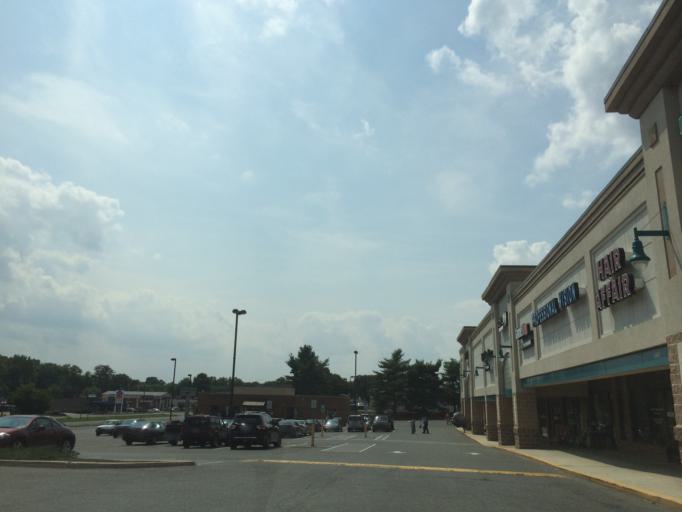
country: US
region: Maryland
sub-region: Howard County
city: Ellicott City
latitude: 39.2780
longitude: -76.8274
